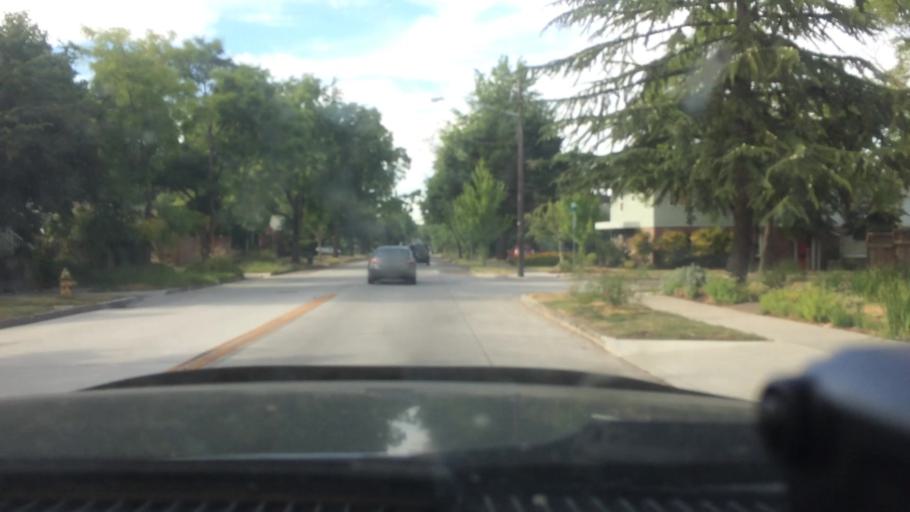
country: US
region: Oregon
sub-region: Lane County
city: Eugene
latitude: 44.0408
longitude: -123.1013
